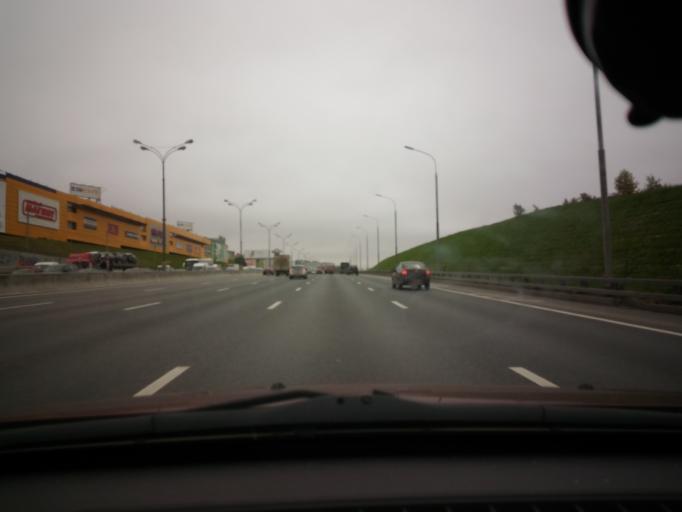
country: RU
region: Moscow
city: Strogino
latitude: 55.8559
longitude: 37.3962
